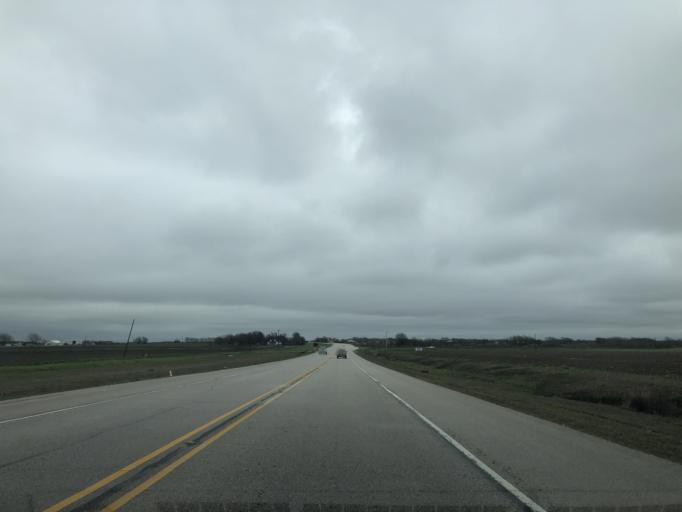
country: US
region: Texas
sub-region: Williamson County
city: Hutto
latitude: 30.6014
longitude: -97.5100
